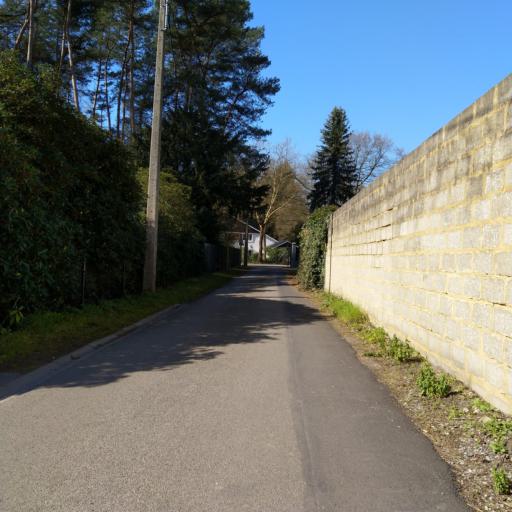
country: BE
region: Wallonia
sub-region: Province du Hainaut
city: Jurbise
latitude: 50.5009
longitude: 3.9345
